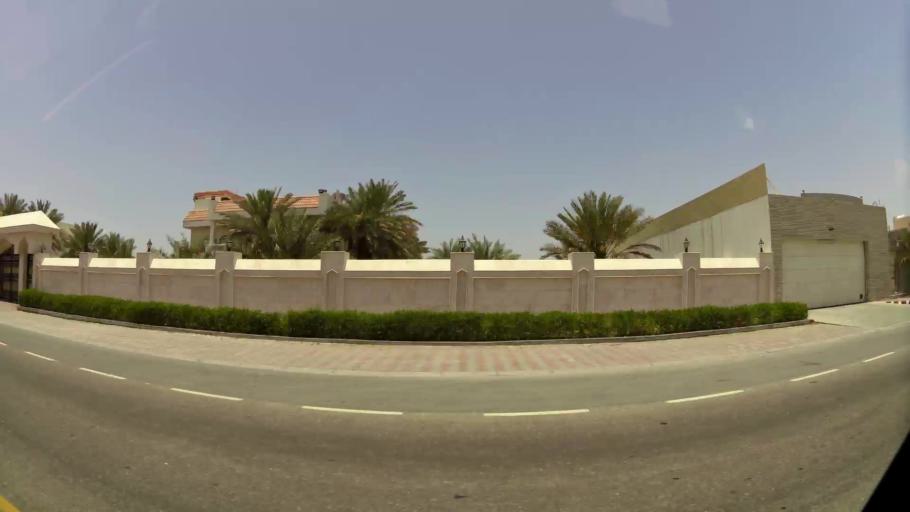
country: AE
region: Dubai
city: Dubai
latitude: 25.1786
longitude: 55.2300
